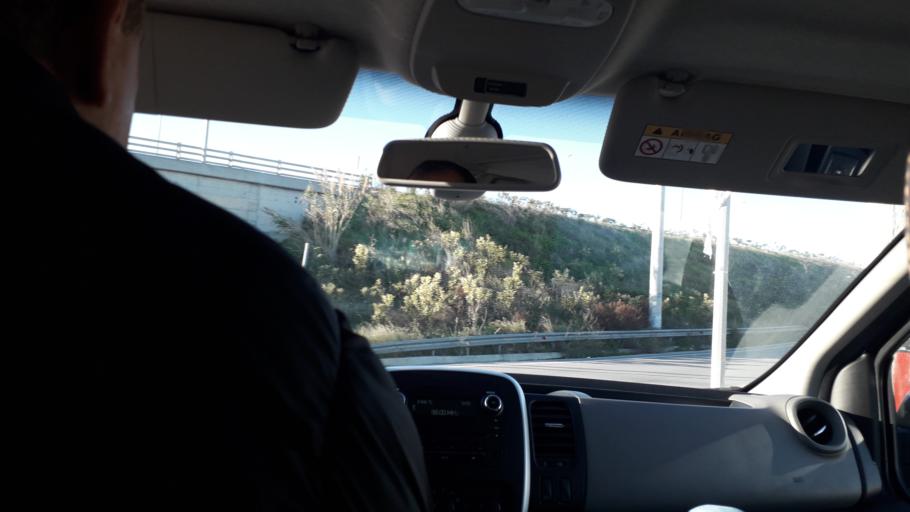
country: GR
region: Crete
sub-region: Nomos Rethymnis
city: Rethymno
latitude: 35.3656
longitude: 24.5154
